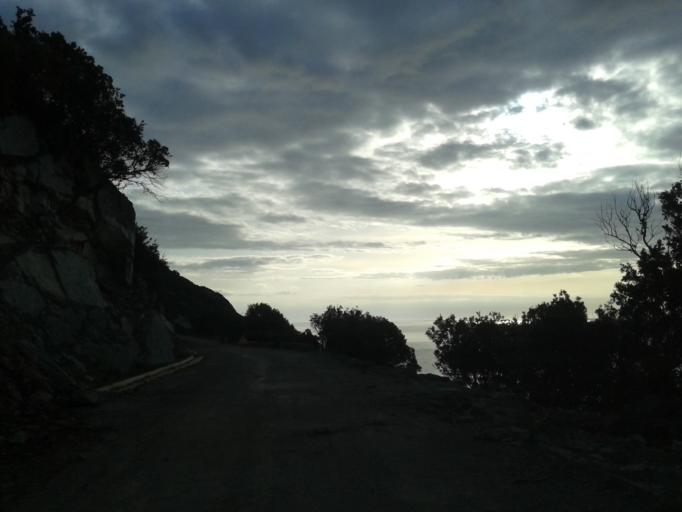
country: FR
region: Corsica
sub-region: Departement de la Haute-Corse
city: Brando
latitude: 42.9025
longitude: 9.3312
